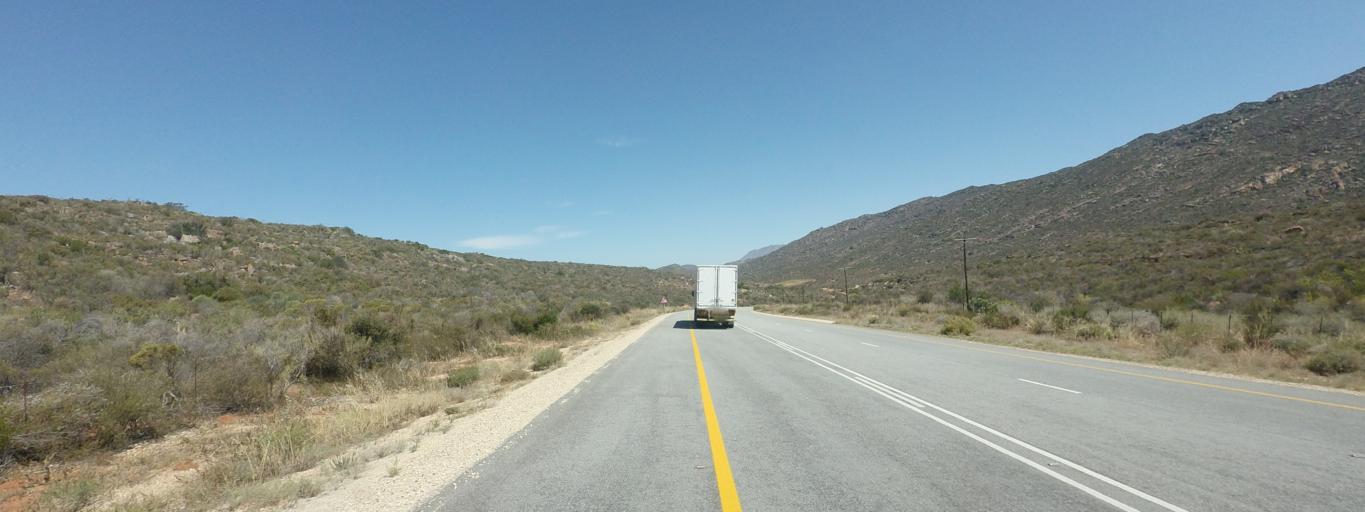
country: ZA
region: Western Cape
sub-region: West Coast District Municipality
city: Clanwilliam
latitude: -32.3324
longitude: 18.9246
